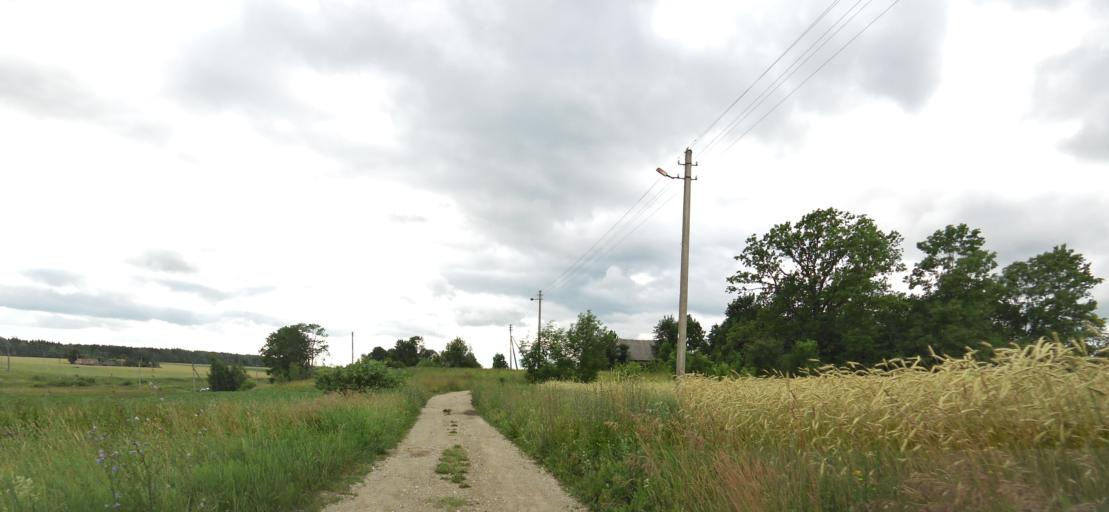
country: LT
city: Obeliai
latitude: 56.0703
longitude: 25.1048
